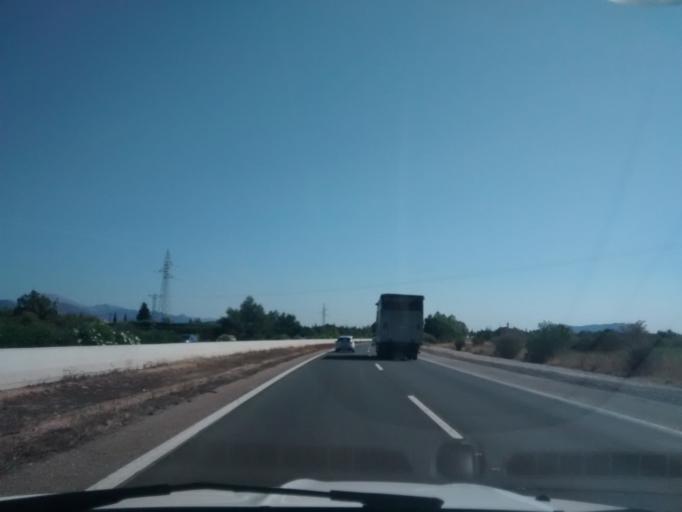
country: ES
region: Balearic Islands
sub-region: Illes Balears
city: Binissalem
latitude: 39.6872
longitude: 2.8611
